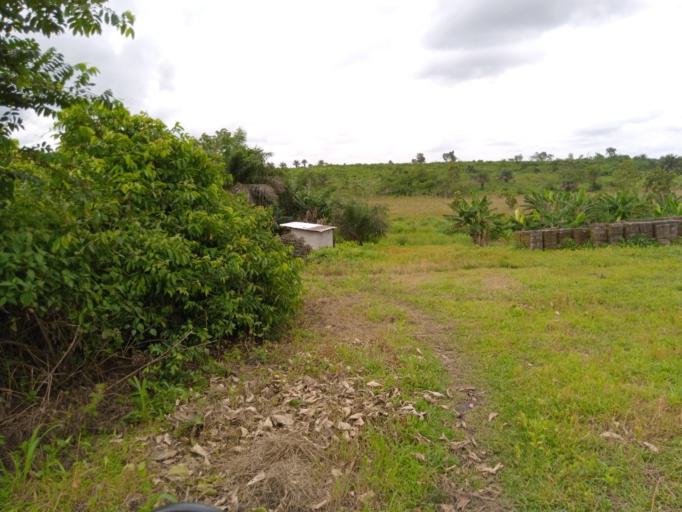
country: SL
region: Southern Province
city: Moyamba
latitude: 8.1651
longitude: -12.4183
